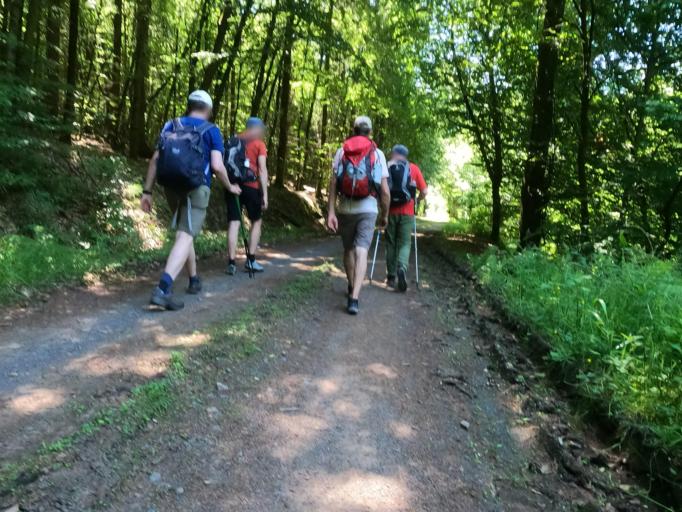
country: DE
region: Rheinland-Pfalz
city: Alpenrod
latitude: 50.6564
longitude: 7.8698
